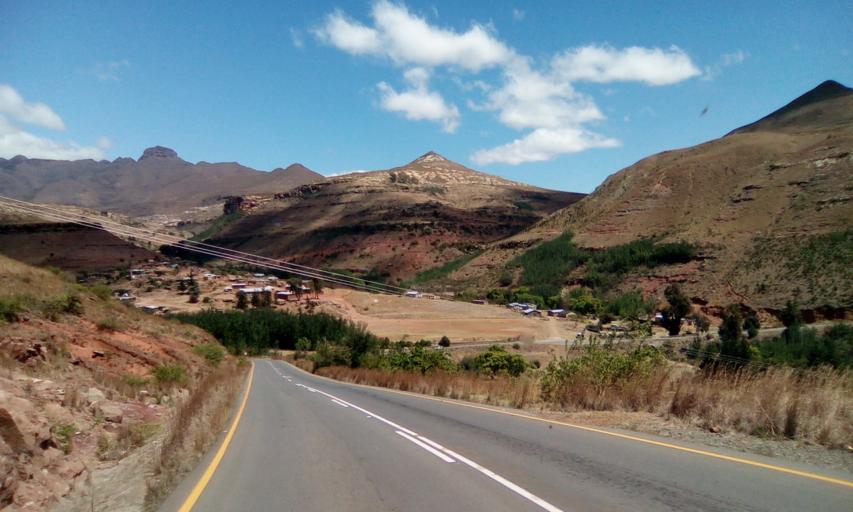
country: LS
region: Qacha's Nek
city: Qacha's Nek
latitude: -30.0794
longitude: 28.6245
